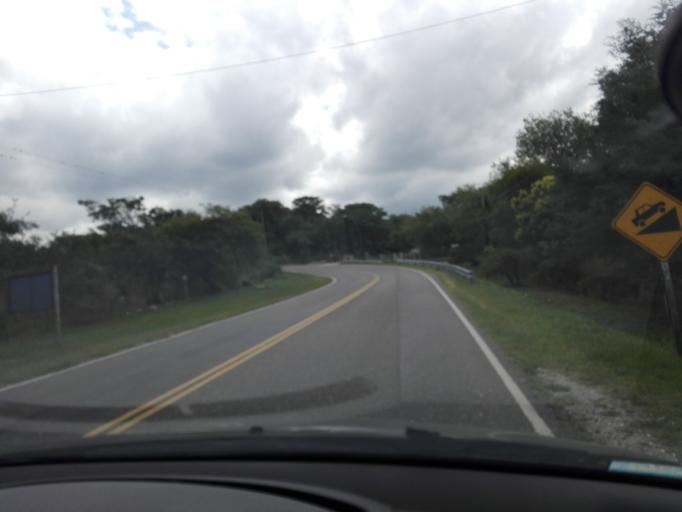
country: AR
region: Cordoba
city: Alta Gracia
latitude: -31.5864
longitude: -64.4619
